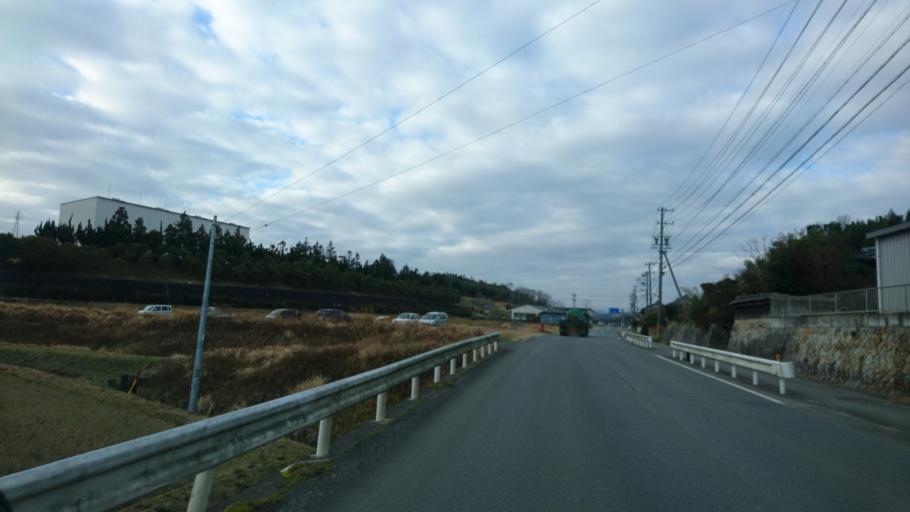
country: JP
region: Mie
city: Ueno-ebisumachi
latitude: 34.7281
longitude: 136.0853
